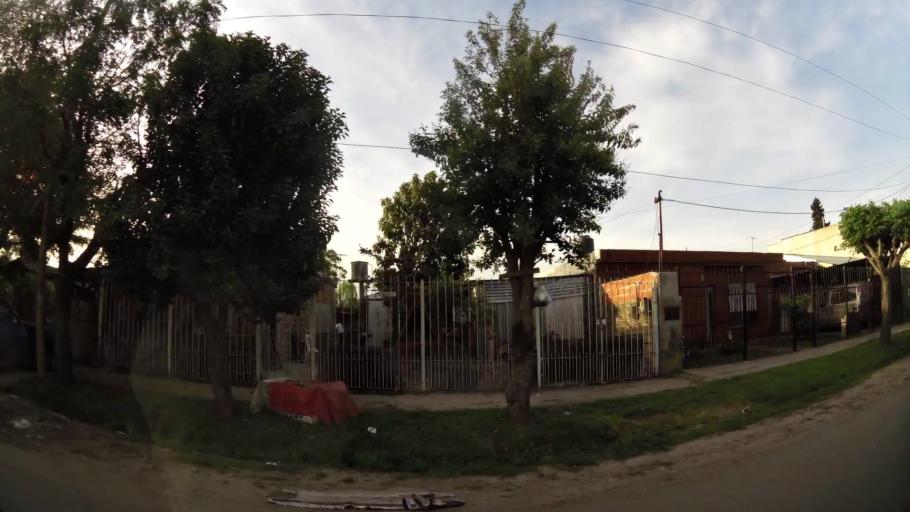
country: AR
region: Buenos Aires
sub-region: Partido de Almirante Brown
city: Adrogue
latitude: -34.7851
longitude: -58.3333
